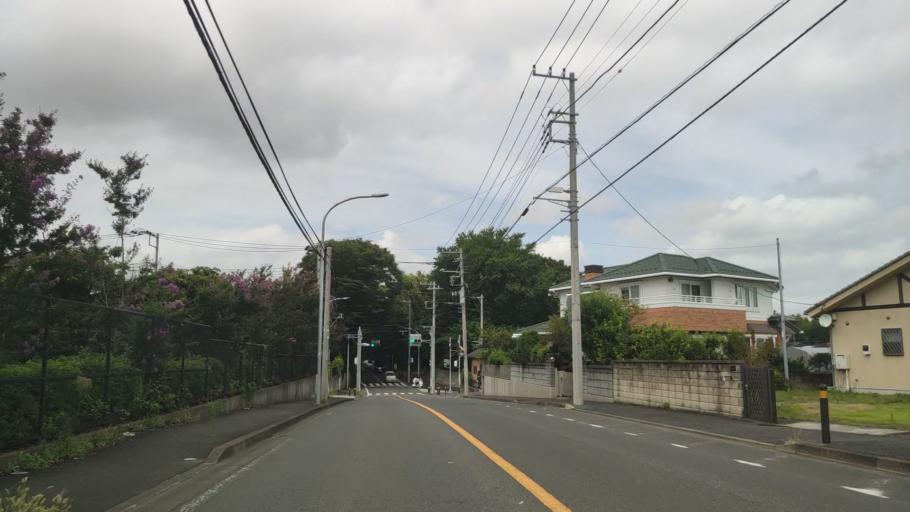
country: JP
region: Kanagawa
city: Minami-rinkan
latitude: 35.4829
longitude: 139.4750
